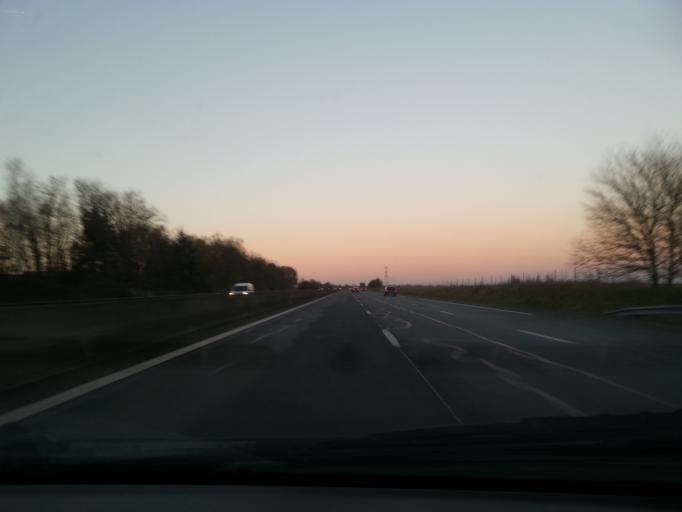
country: FR
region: Centre
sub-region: Departement d'Eure-et-Loir
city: Morancez
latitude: 48.4020
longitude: 1.4990
